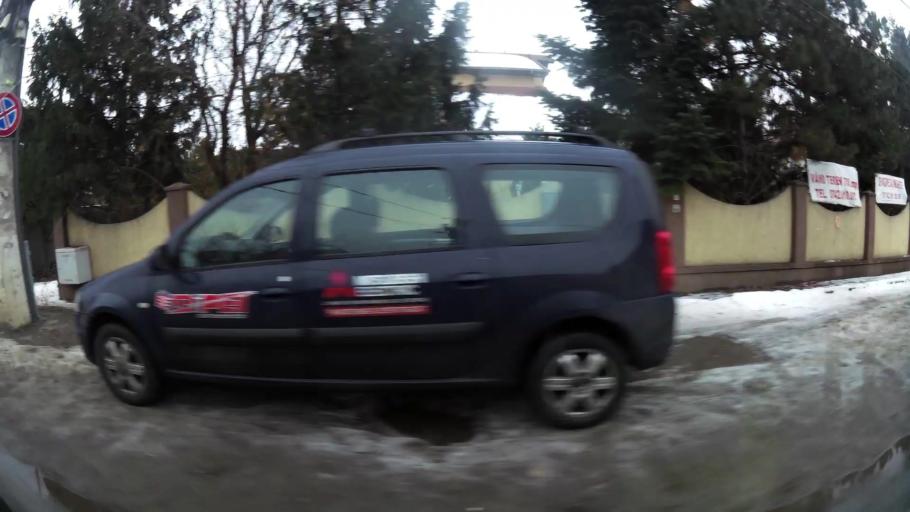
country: RO
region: Ilfov
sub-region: Comuna Chiajna
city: Rosu
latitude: 44.4496
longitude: 26.0010
